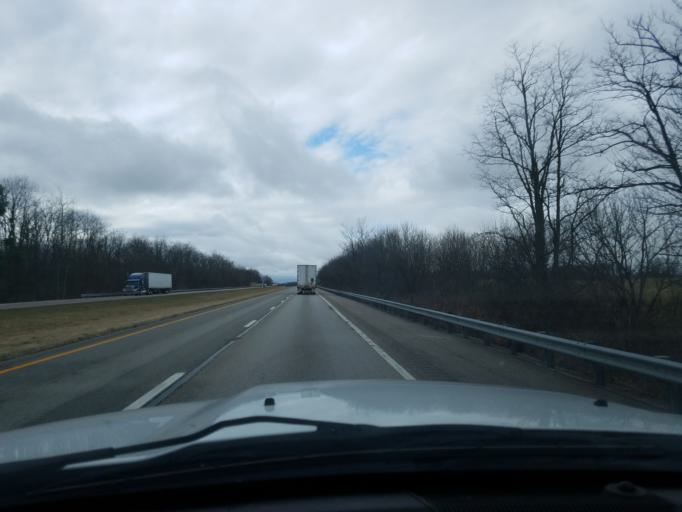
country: US
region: Kentucky
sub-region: Clark County
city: Winchester
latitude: 38.0233
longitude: -84.1304
